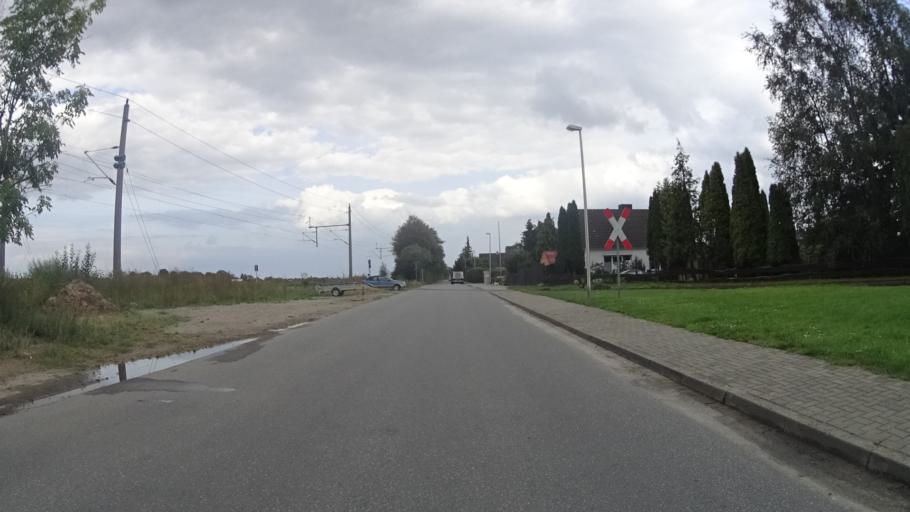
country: DE
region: Schleswig-Holstein
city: Gluckstadt
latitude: 53.7840
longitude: 9.4370
